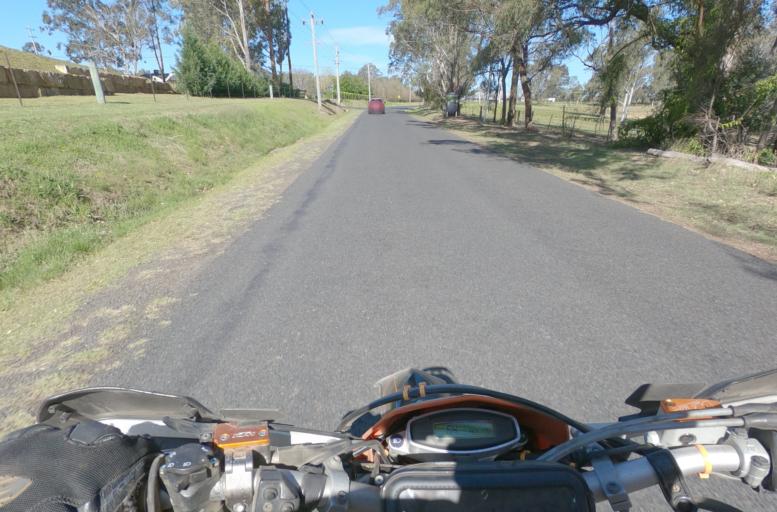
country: AU
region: New South Wales
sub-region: Hawkesbury
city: Scheyville
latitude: -33.5623
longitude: 150.9110
